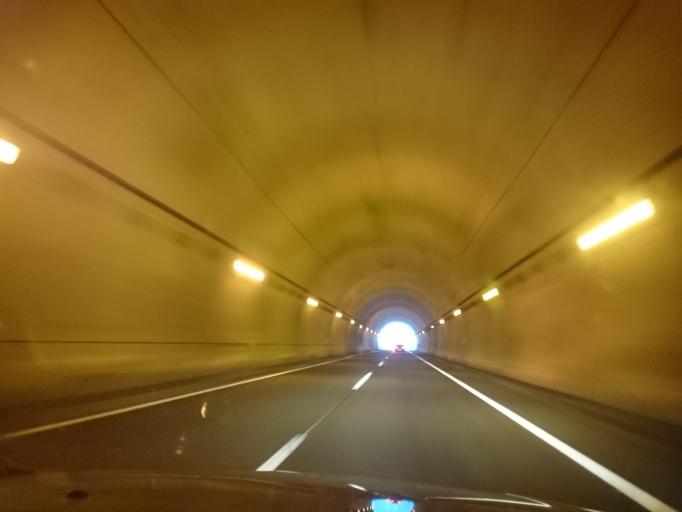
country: ES
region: Castille and Leon
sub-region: Provincia de Leon
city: Sena de Luna
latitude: 42.9949
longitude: -5.8159
